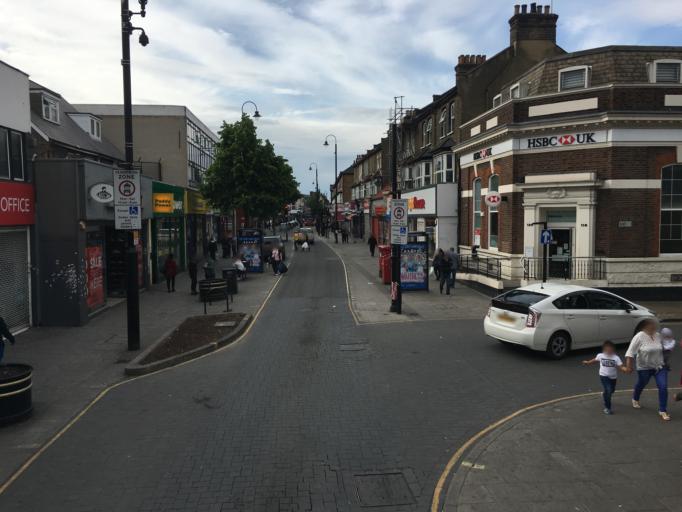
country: GB
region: England
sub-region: Greater London
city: East Ham
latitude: 51.5365
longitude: 0.0522
